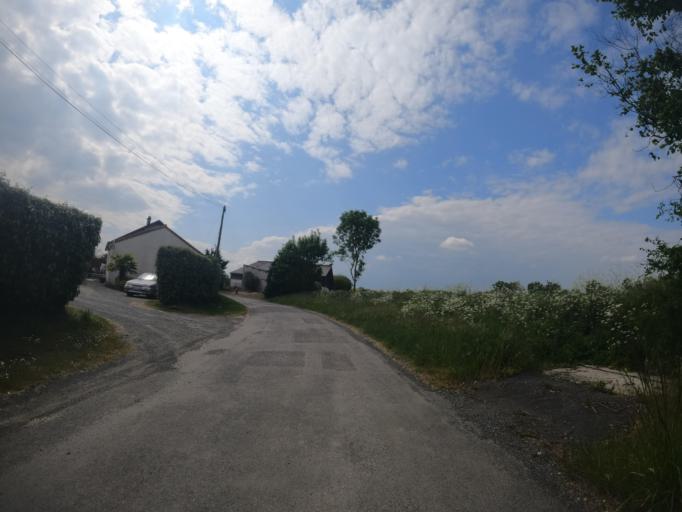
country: FR
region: Poitou-Charentes
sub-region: Departement des Deux-Sevres
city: Saint-Varent
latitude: 46.8930
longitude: -0.2907
